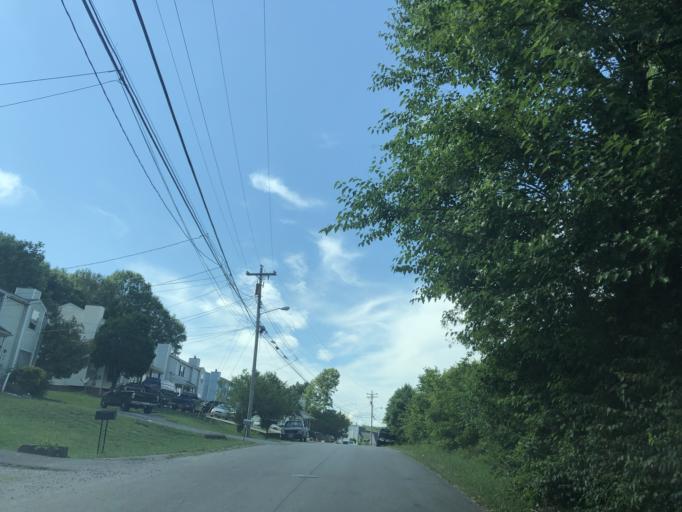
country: US
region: Tennessee
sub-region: Davidson County
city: Nashville
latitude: 36.2390
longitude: -86.8078
